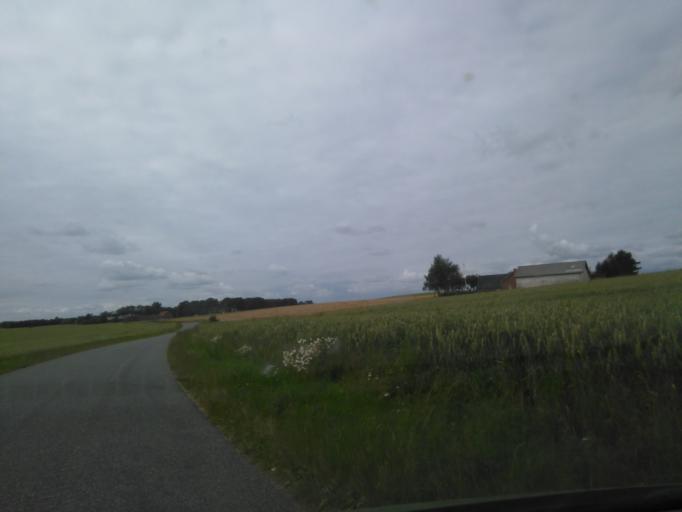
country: DK
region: Central Jutland
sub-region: Arhus Kommune
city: Solbjerg
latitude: 56.0132
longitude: 10.0670
